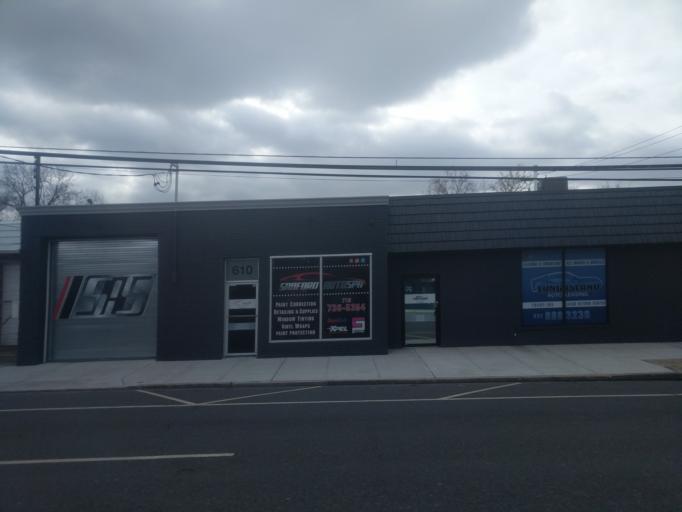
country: US
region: New York
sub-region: Nassau County
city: Lynbrook
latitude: 40.6609
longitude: -73.6844
